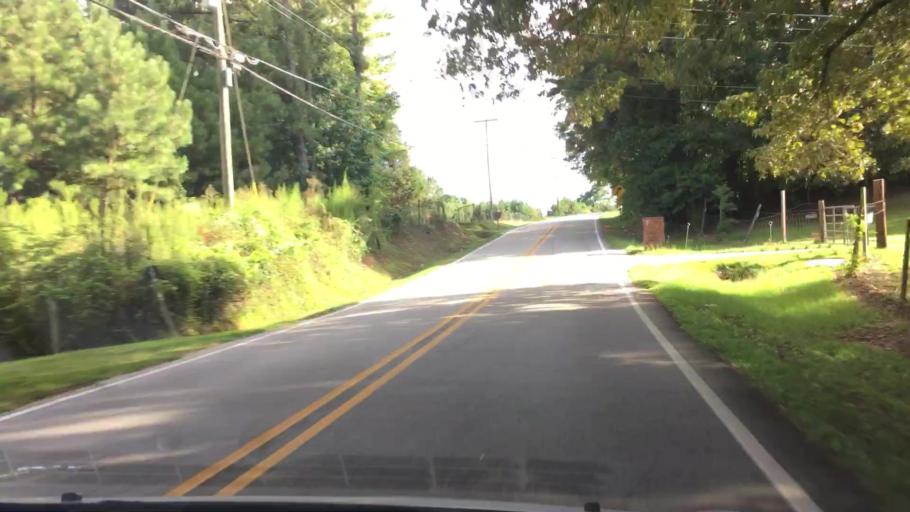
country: US
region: Georgia
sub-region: Henry County
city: Stockbridge
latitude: 33.5936
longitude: -84.1896
